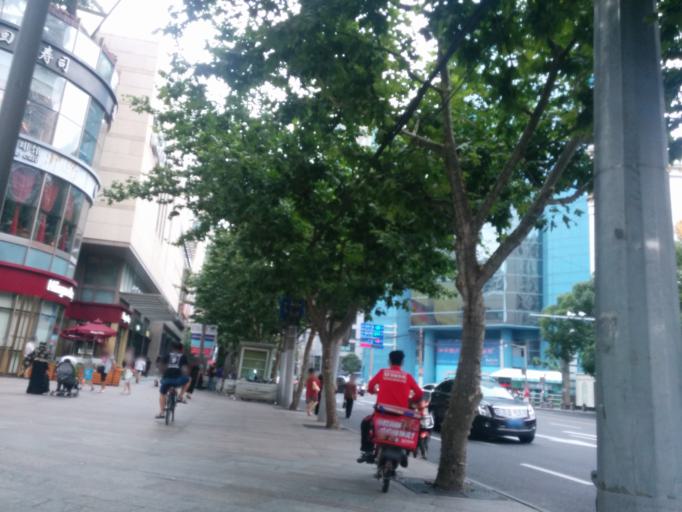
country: CN
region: Shanghai Shi
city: Changning
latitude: 31.2311
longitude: 121.4234
